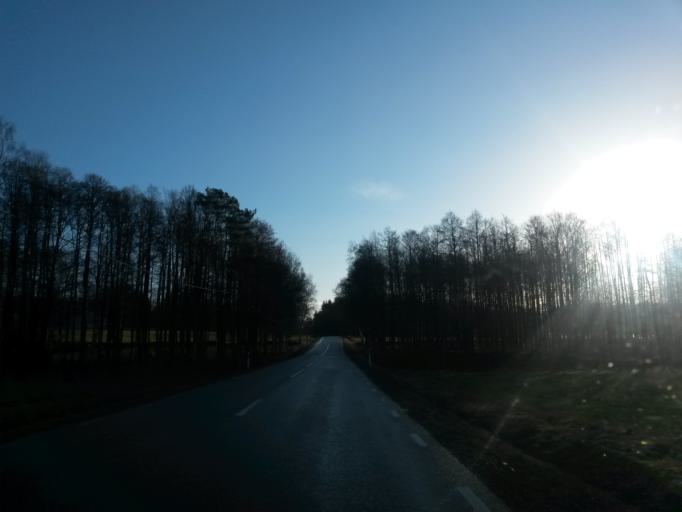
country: SE
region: Vaestra Goetaland
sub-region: Vargarda Kommun
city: Vargarda
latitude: 57.9296
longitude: 12.8573
